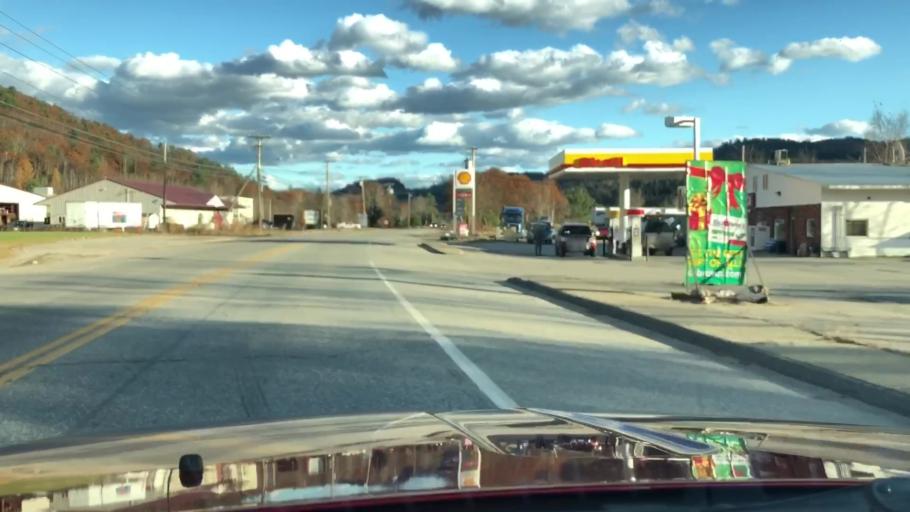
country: US
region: Maine
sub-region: Oxford County
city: Mexico
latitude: 44.5360
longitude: -70.5095
